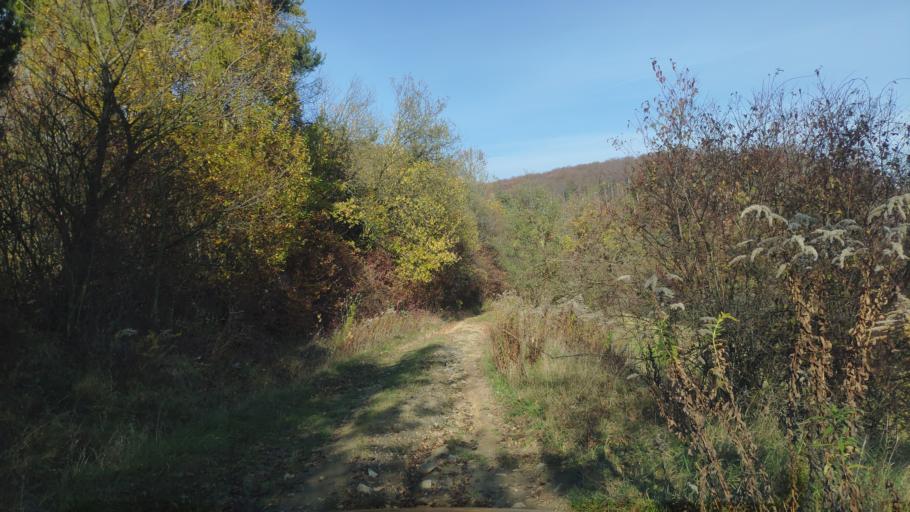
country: SK
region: Presovsky
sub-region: Okres Presov
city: Presov
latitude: 48.9008
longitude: 21.2223
